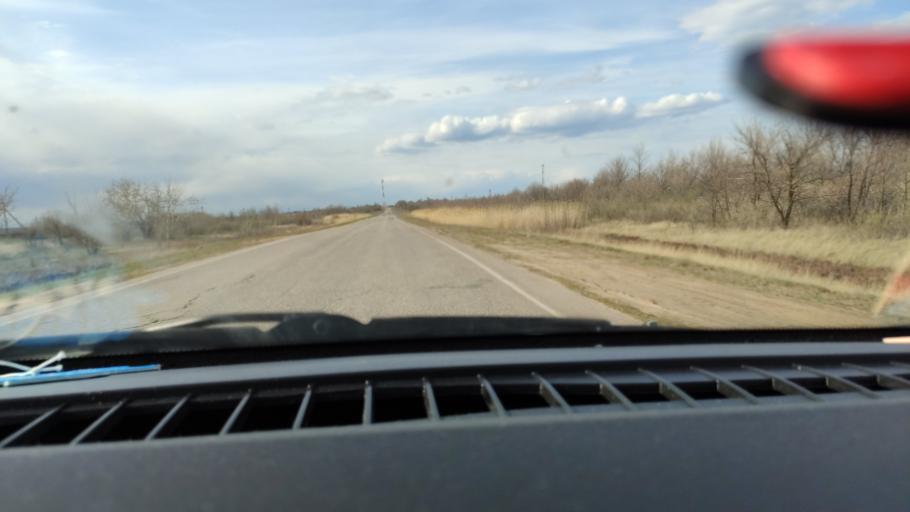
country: RU
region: Saratov
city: Rovnoye
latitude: 51.0127
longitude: 46.0973
